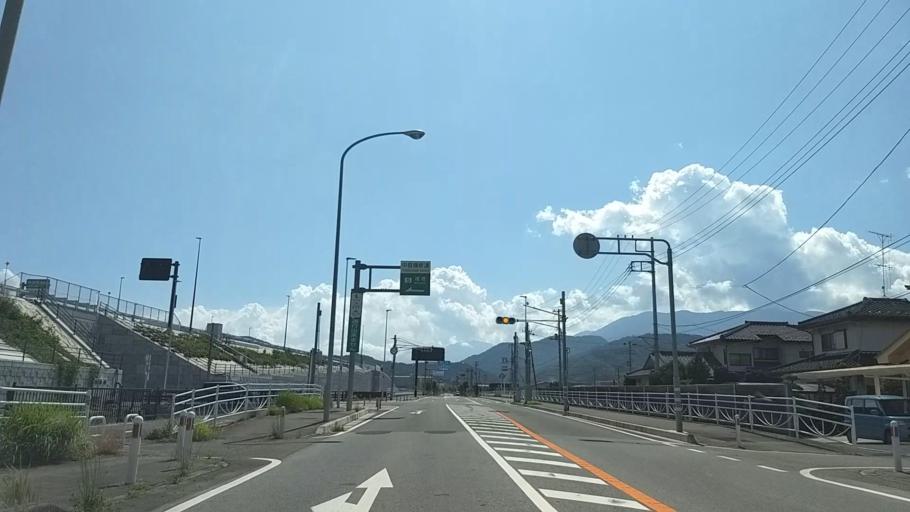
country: JP
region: Yamanashi
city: Ryuo
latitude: 35.5603
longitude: 138.4718
